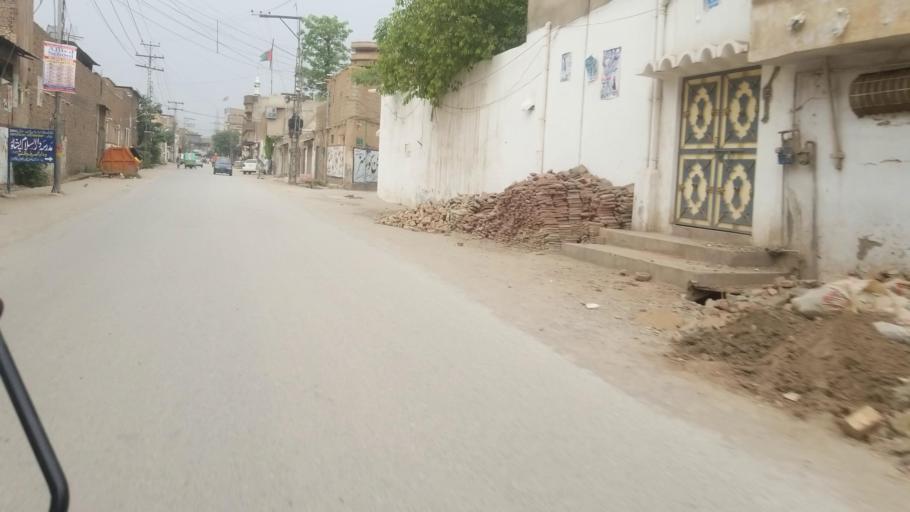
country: PK
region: Khyber Pakhtunkhwa
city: Peshawar
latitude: 33.9841
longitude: 71.5590
